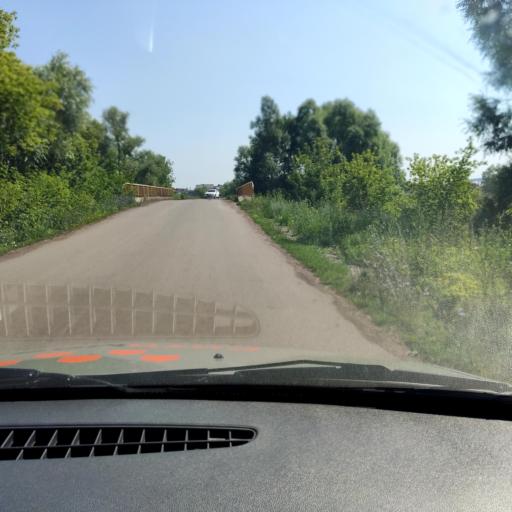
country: RU
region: Bashkortostan
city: Ufa
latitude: 54.6102
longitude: 55.9015
